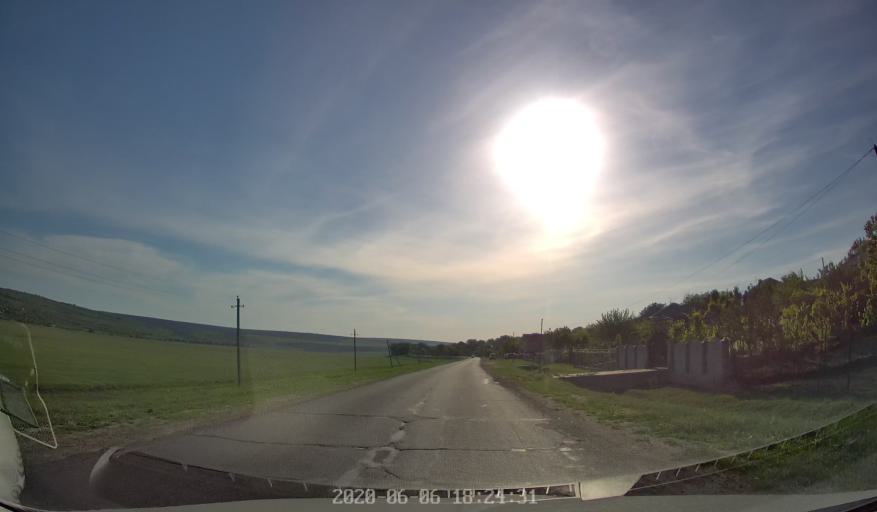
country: MD
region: Chisinau
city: Vadul lui Voda
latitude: 47.1168
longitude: 29.0507
